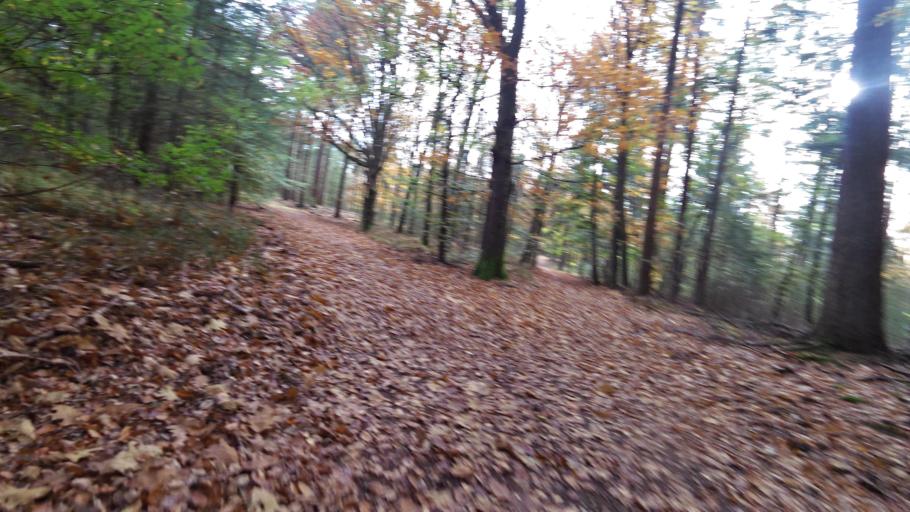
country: NL
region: Gelderland
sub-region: Gemeente Epe
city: Emst
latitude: 52.3396
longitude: 5.9201
